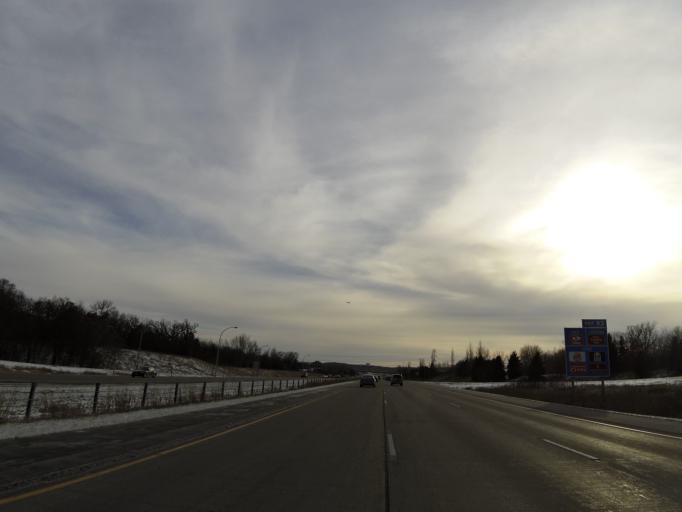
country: US
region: Minnesota
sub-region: Dakota County
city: Eagan
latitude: 44.8031
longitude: -93.1917
